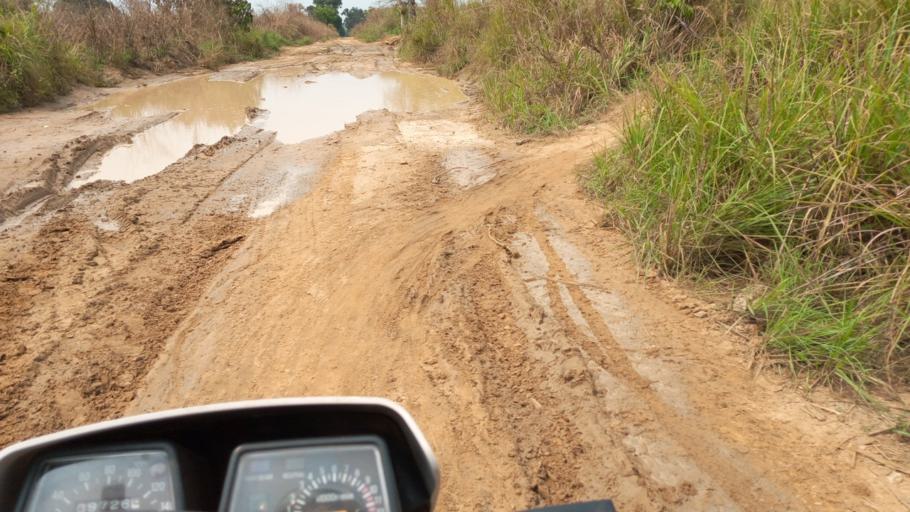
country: CD
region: Bandundu
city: Bandundu
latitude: -3.4846
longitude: 17.7859
